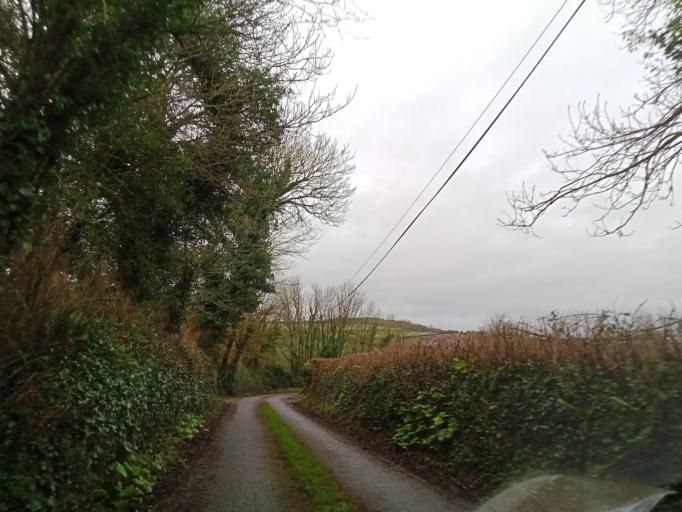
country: IE
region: Munster
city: Fethard
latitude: 52.5613
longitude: -7.7137
